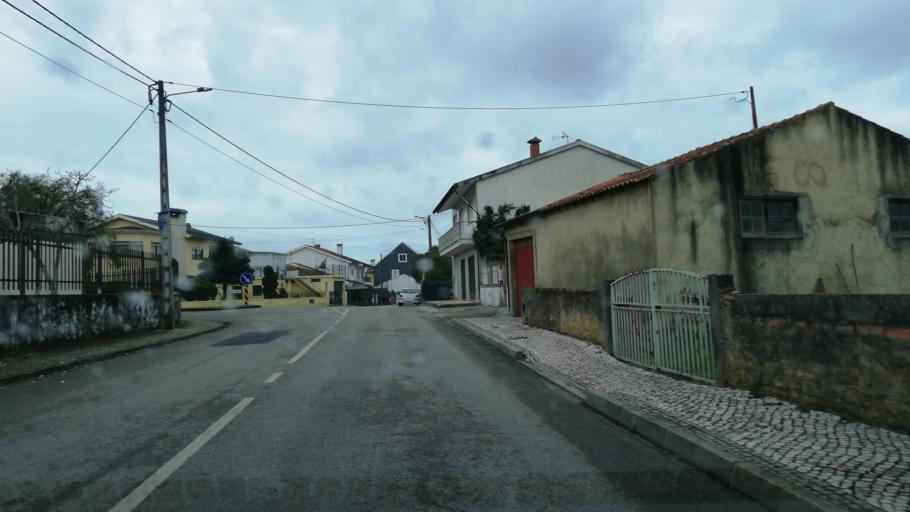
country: PT
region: Aveiro
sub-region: Agueda
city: Valongo
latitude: 40.6168
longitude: -8.4325
